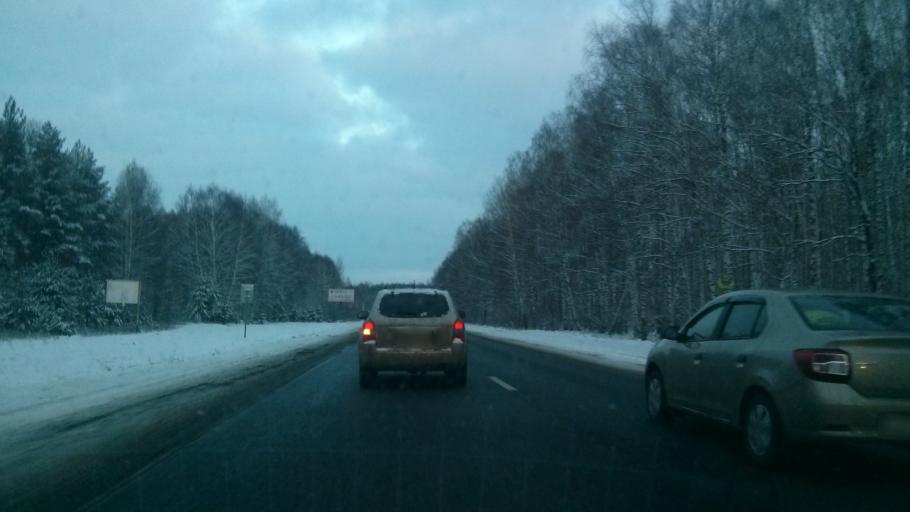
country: RU
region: Nizjnij Novgorod
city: Vorsma
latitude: 56.0103
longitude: 43.3361
